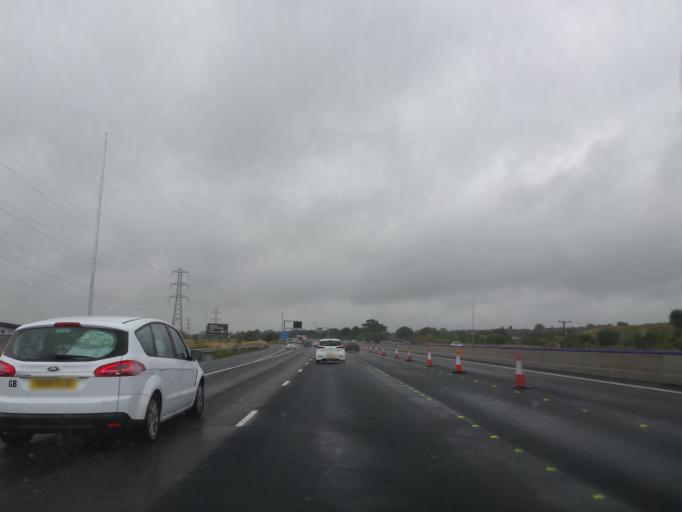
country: GB
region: England
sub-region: Derbyshire
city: Staveley
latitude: 53.2513
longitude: -1.3270
